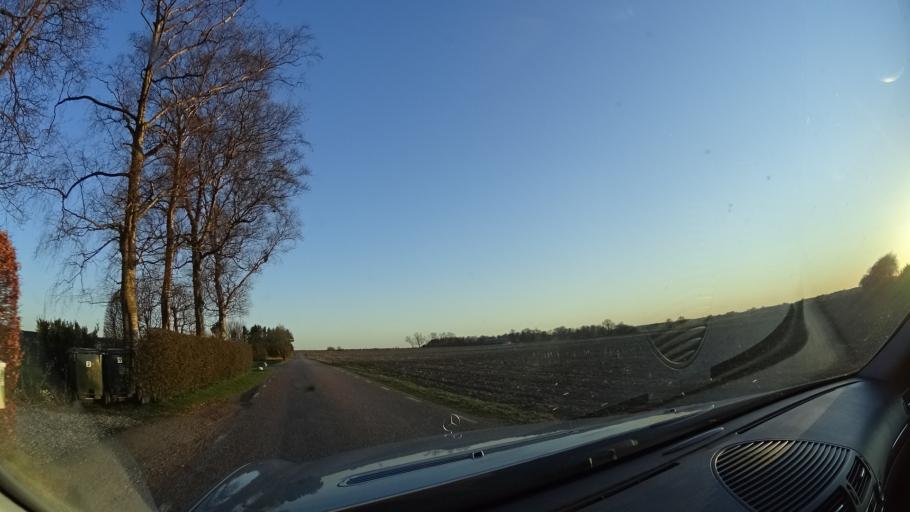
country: SE
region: Skane
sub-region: Eslovs Kommun
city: Stehag
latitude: 55.8577
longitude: 13.4434
